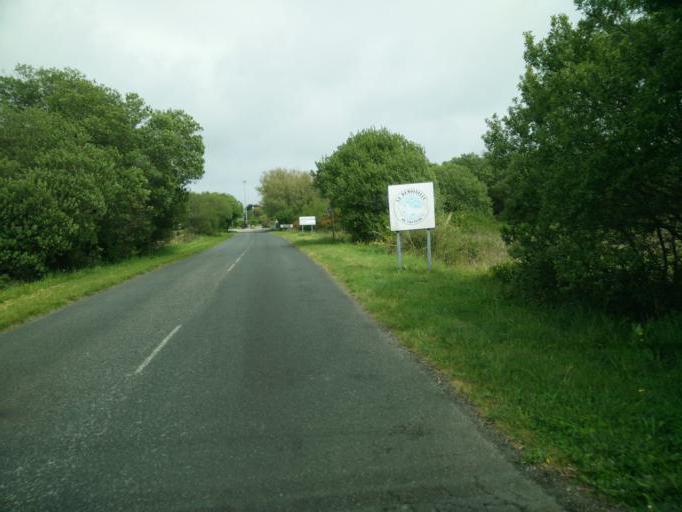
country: FR
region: Brittany
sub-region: Departement du Finistere
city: Plobannalec-Lesconil
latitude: 47.8033
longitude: -4.1973
